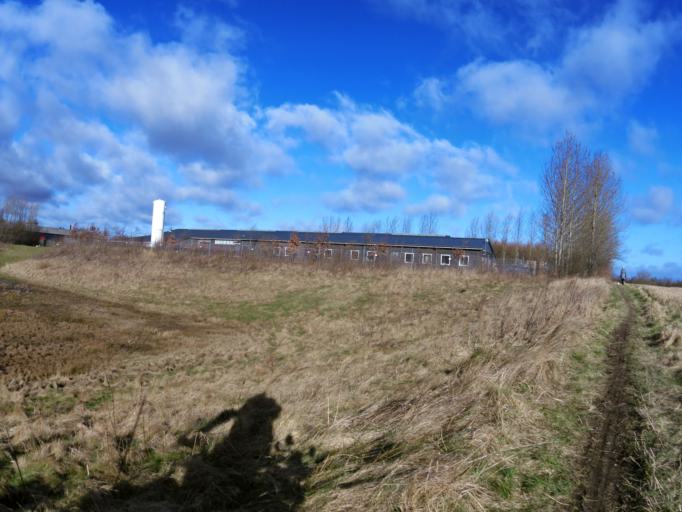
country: DK
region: Central Jutland
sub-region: Arhus Kommune
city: Tranbjerg
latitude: 56.1029
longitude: 10.1251
